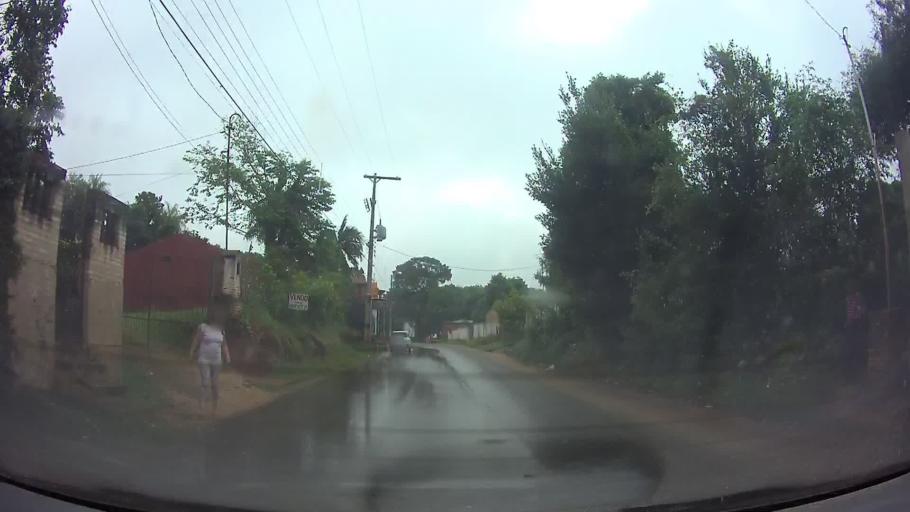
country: PY
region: Central
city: San Lorenzo
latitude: -25.3289
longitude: -57.5044
